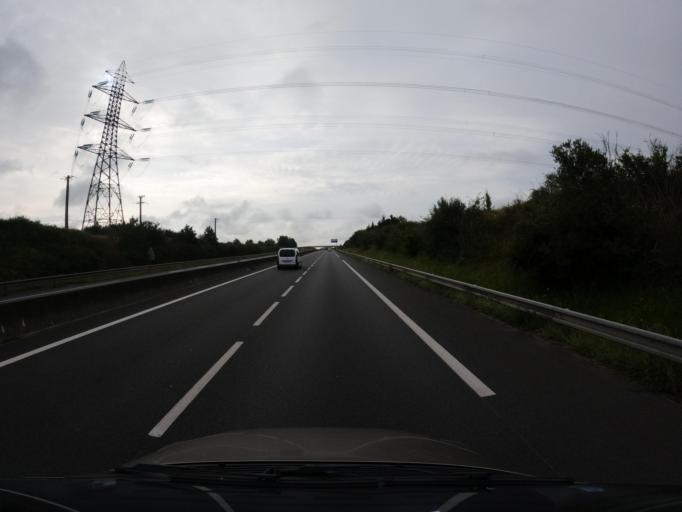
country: FR
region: Centre
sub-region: Departement d'Indre-et-Loire
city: Villandry
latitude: 47.3148
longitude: 0.5053
